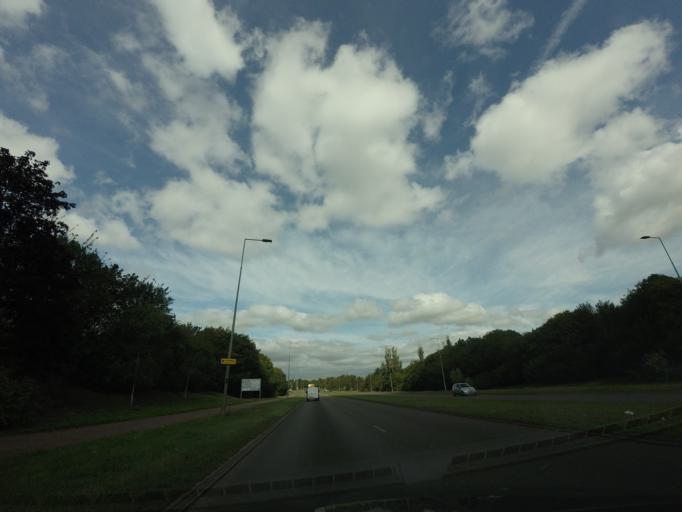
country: GB
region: England
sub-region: Milton Keynes
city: Broughton
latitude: 52.0426
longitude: -0.6957
